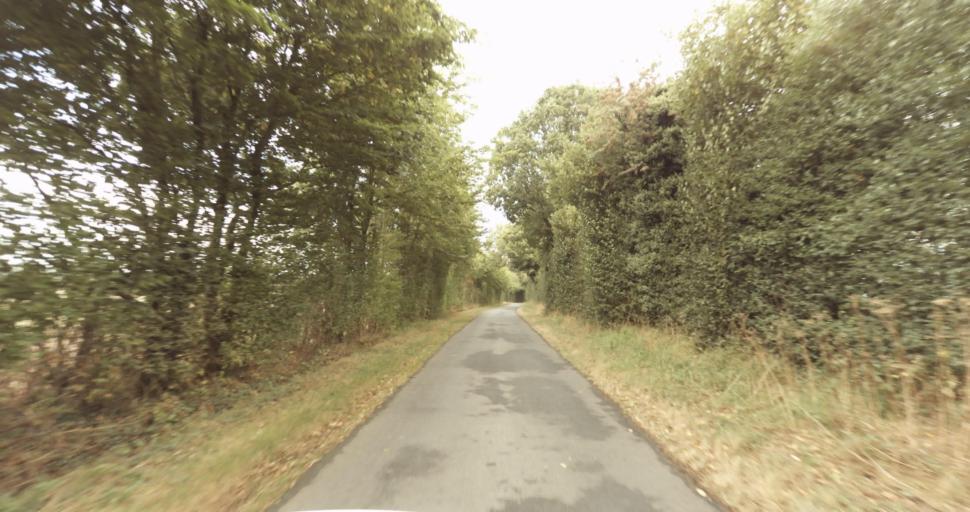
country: FR
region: Lower Normandy
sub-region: Departement de l'Orne
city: Vimoutiers
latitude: 48.9378
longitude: 0.1432
